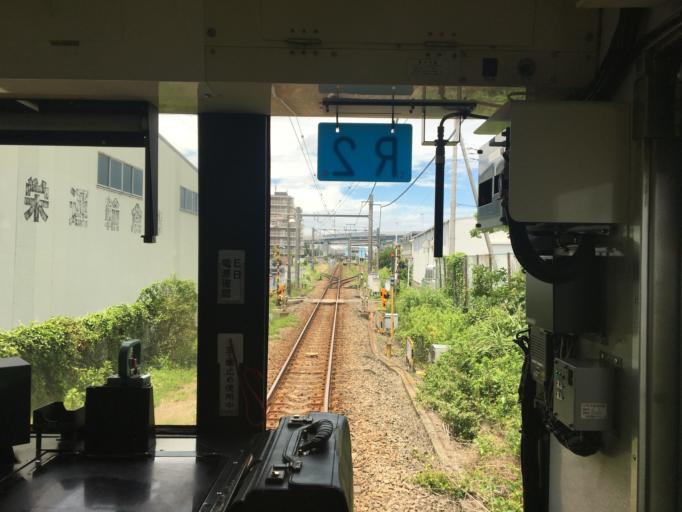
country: JP
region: Kanagawa
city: Atsugi
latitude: 35.4179
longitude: 139.3774
